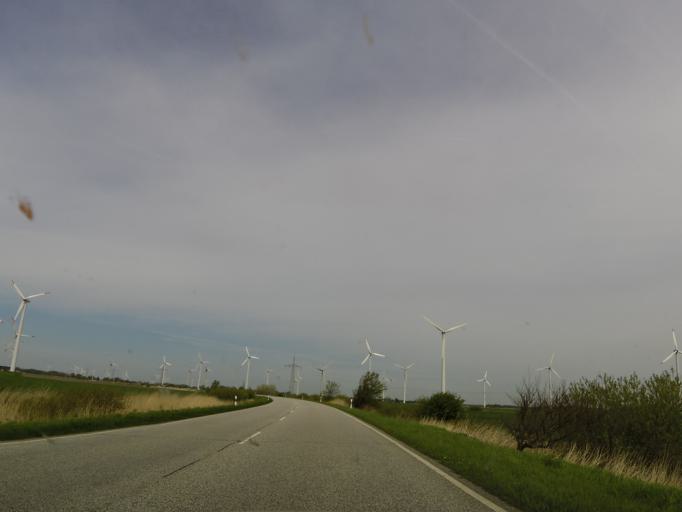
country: DE
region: Schleswig-Holstein
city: Stelle-Wittenwurth
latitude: 54.2588
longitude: 9.0357
